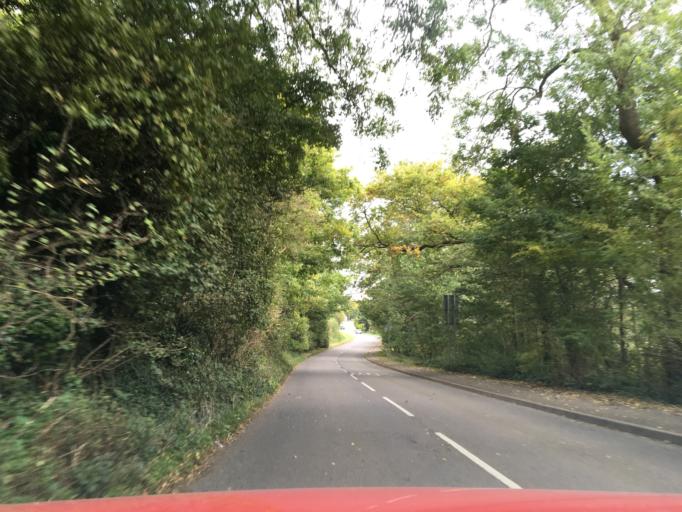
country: GB
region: England
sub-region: South Gloucestershire
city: Almondsbury
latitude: 51.5775
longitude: -2.5738
